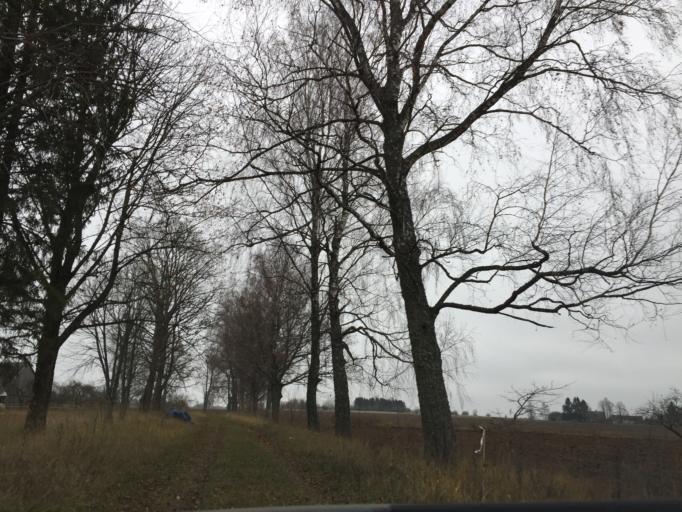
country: LV
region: Limbazu Rajons
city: Limbazi
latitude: 57.4639
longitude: 24.7101
